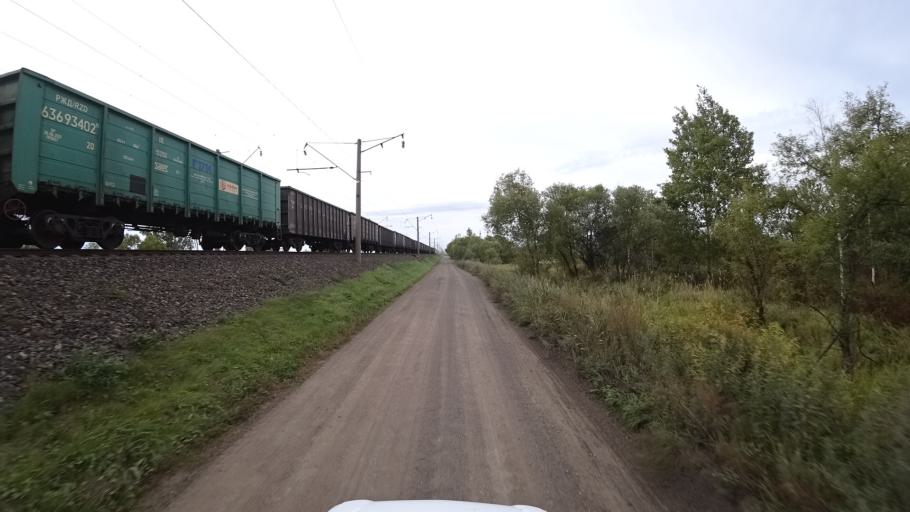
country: RU
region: Amur
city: Arkhara
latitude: 49.3619
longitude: 130.1487
